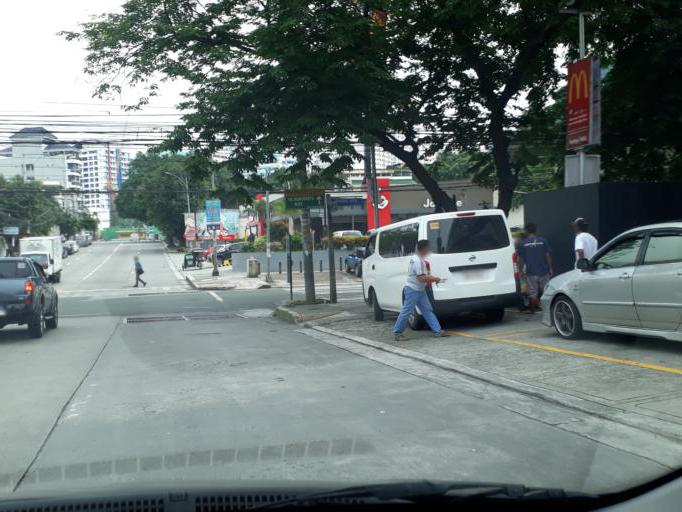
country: PH
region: Calabarzon
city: Del Monte
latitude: 14.6354
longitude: 121.0311
